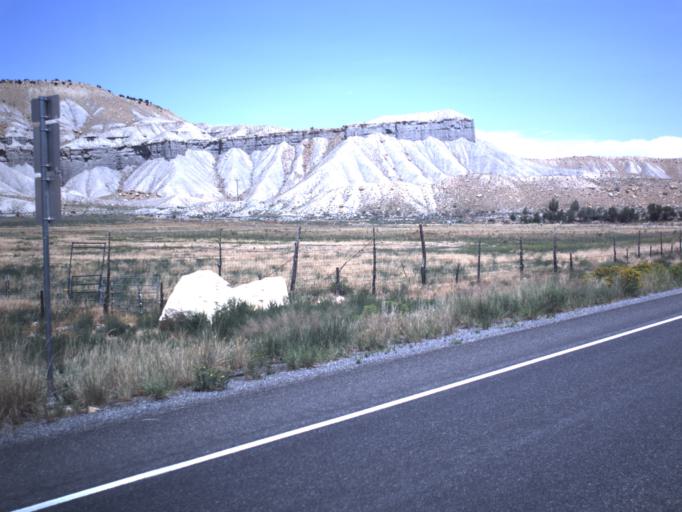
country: US
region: Utah
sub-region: Emery County
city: Huntington
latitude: 39.3622
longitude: -111.0422
